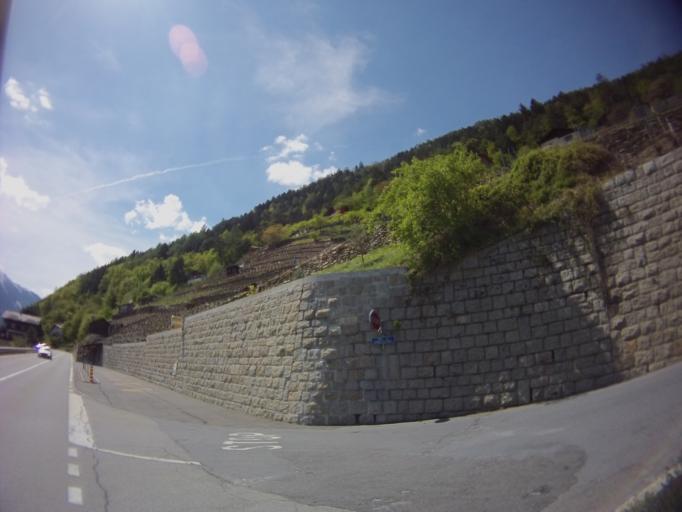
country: CH
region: Valais
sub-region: Martigny District
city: Martigny-Ville
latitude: 46.0984
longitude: 7.0560
